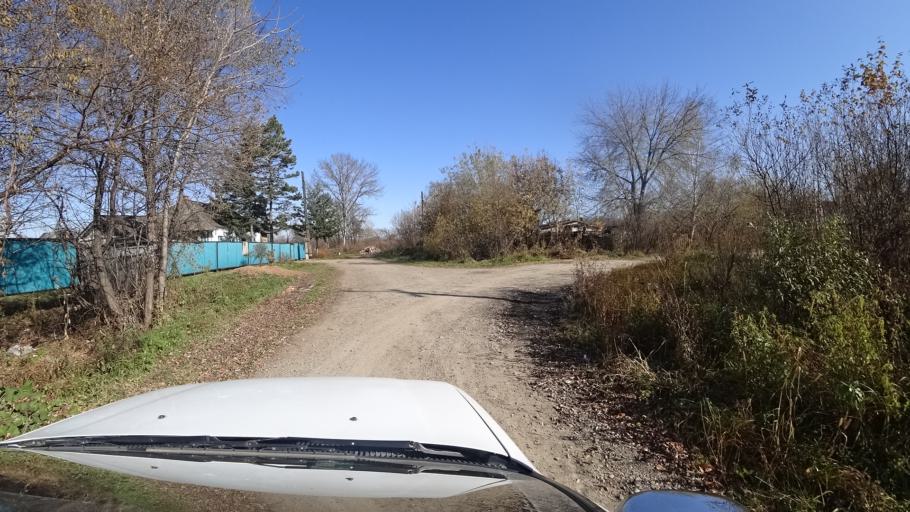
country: RU
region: Primorskiy
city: Dal'nerechensk
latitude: 45.9144
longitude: 133.8013
